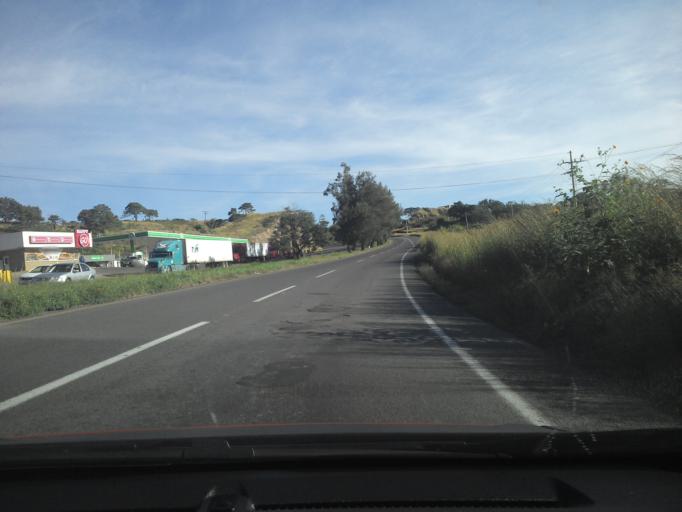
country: MX
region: Jalisco
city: La Venta del Astillero
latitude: 20.7350
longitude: -103.5785
